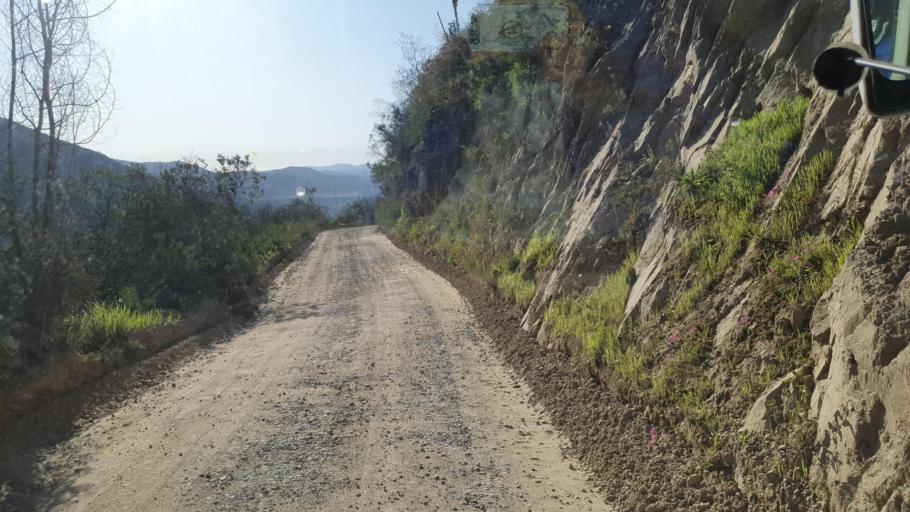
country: CL
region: Valparaiso
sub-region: Provincia de Marga Marga
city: Limache
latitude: -33.2045
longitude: -71.2573
